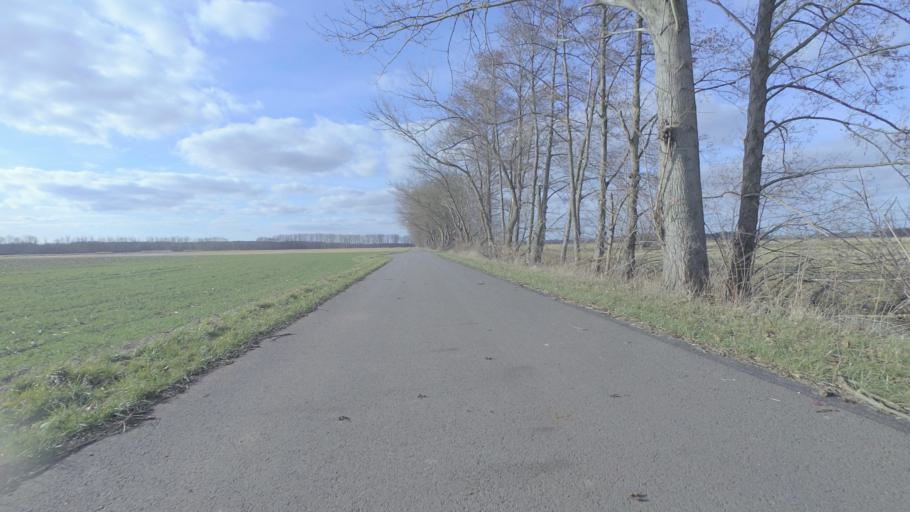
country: DE
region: Brandenburg
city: Trebbin
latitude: 52.2221
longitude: 13.2708
